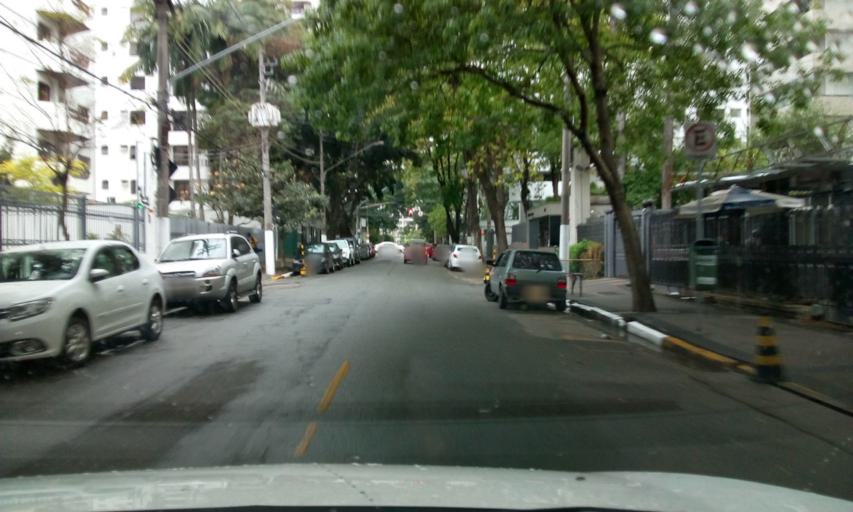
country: BR
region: Sao Paulo
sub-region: Sao Paulo
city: Sao Paulo
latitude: -23.5931
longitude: -46.6704
